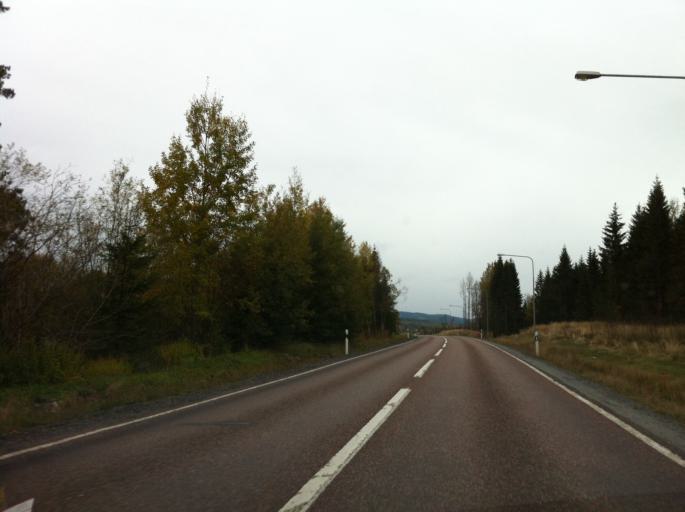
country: SE
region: Dalarna
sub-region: Ludvika Kommun
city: Grangesberg
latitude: 60.0168
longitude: 14.9850
